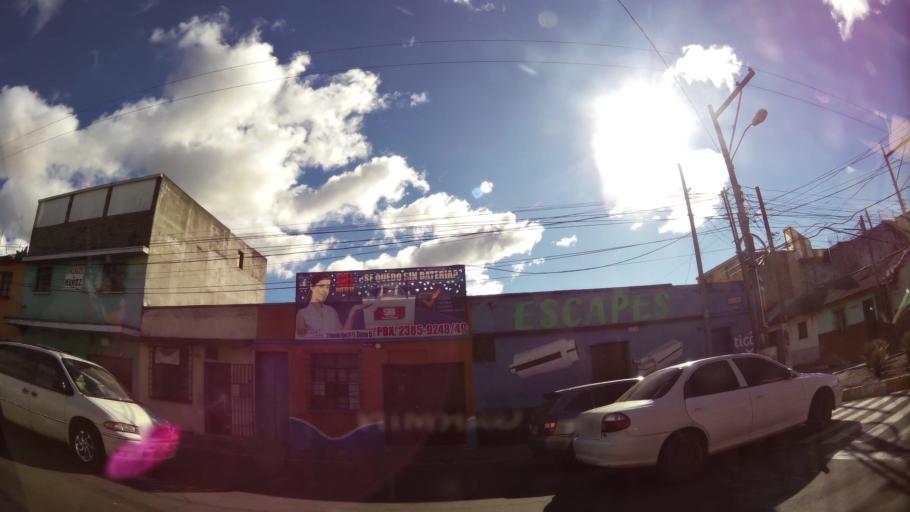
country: GT
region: Guatemala
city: Guatemala City
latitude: 14.6179
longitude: -90.5027
